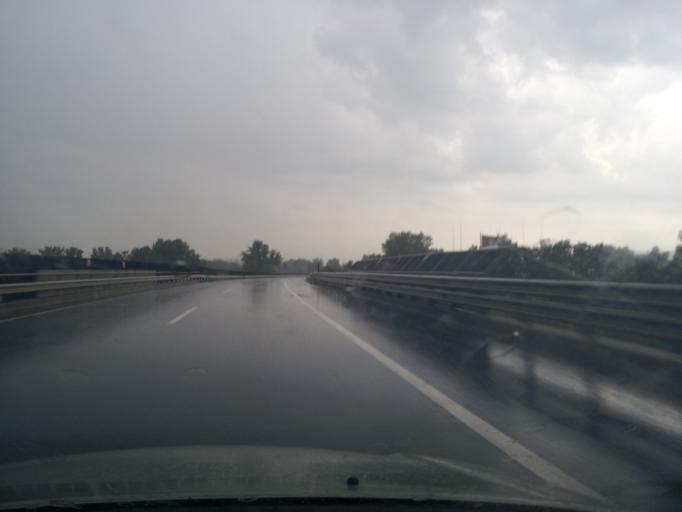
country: HU
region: Borsod-Abauj-Zemplen
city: Felsozsolca
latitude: 48.0878
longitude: 20.8514
